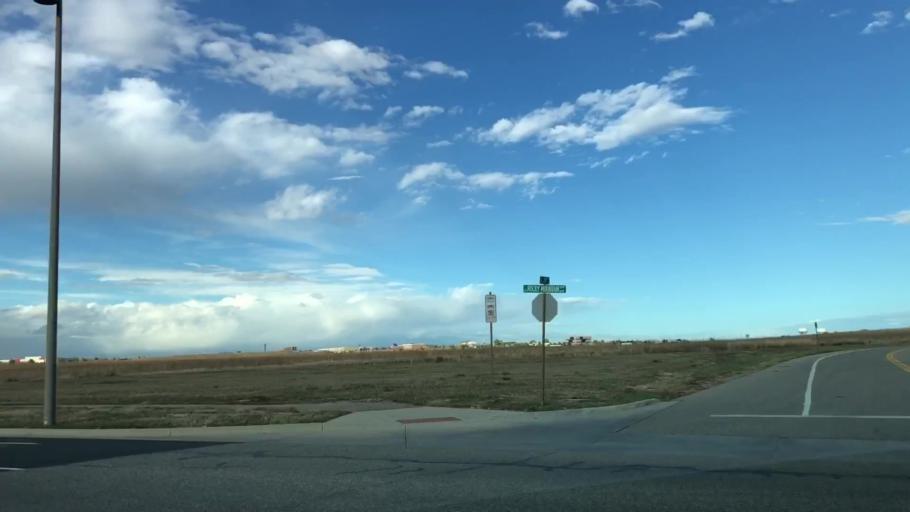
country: US
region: Colorado
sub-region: Larimer County
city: Loveland
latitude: 40.4197
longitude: -105.0014
